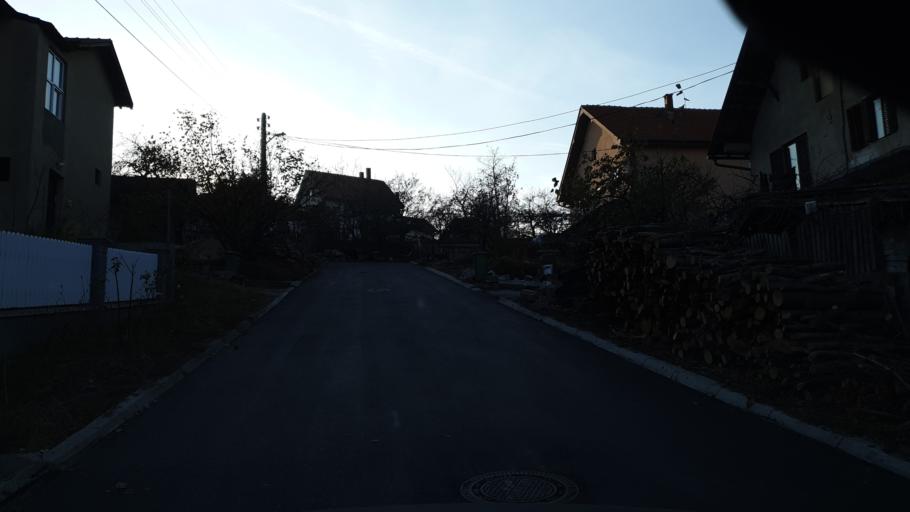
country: RS
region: Central Serbia
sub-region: Borski Okrug
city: Bor
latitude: 44.0526
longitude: 22.0884
